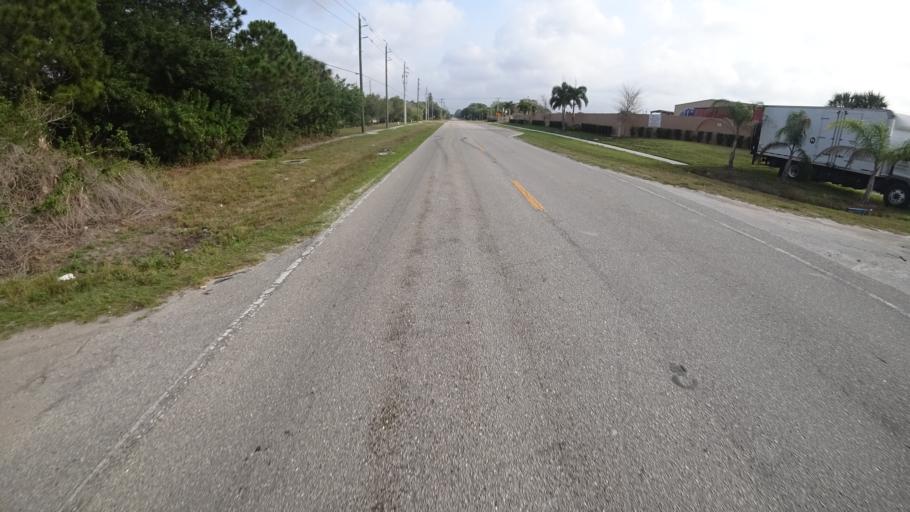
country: US
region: Florida
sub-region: Manatee County
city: Samoset
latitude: 27.4272
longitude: -82.5219
